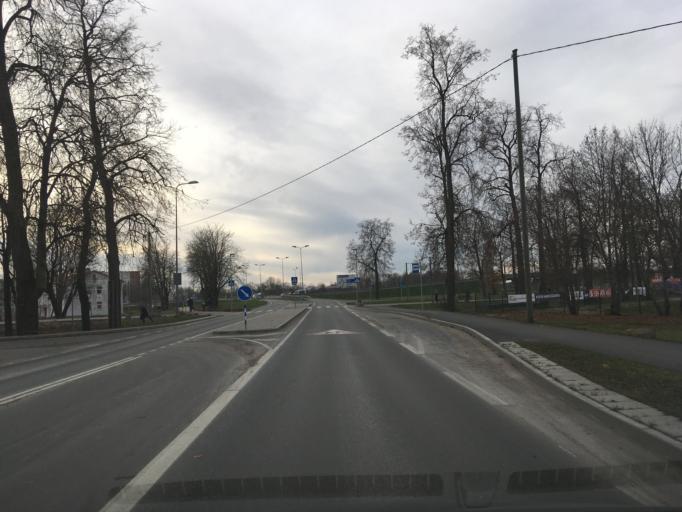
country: EE
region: Ida-Virumaa
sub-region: Johvi vald
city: Johvi
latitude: 59.3550
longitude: 27.4204
